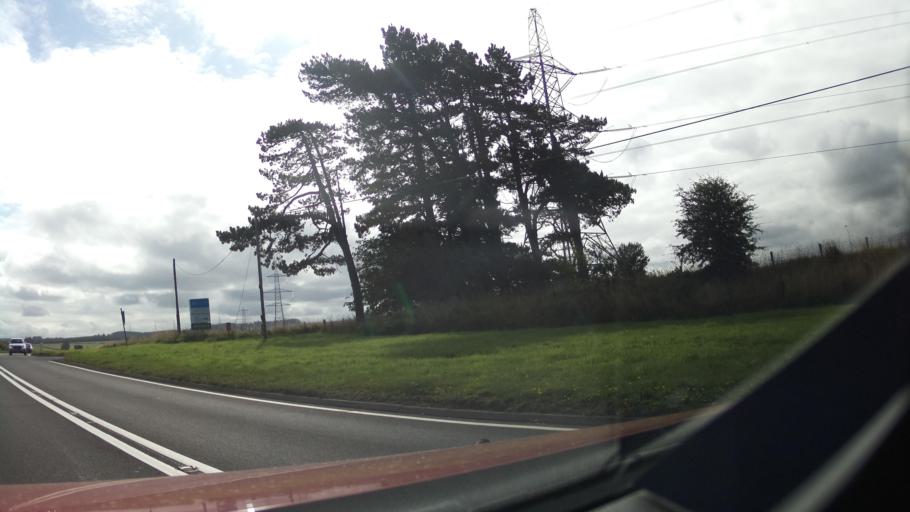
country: GB
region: Scotland
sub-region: Fife
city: Pathhead
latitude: 55.8450
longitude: -2.9270
